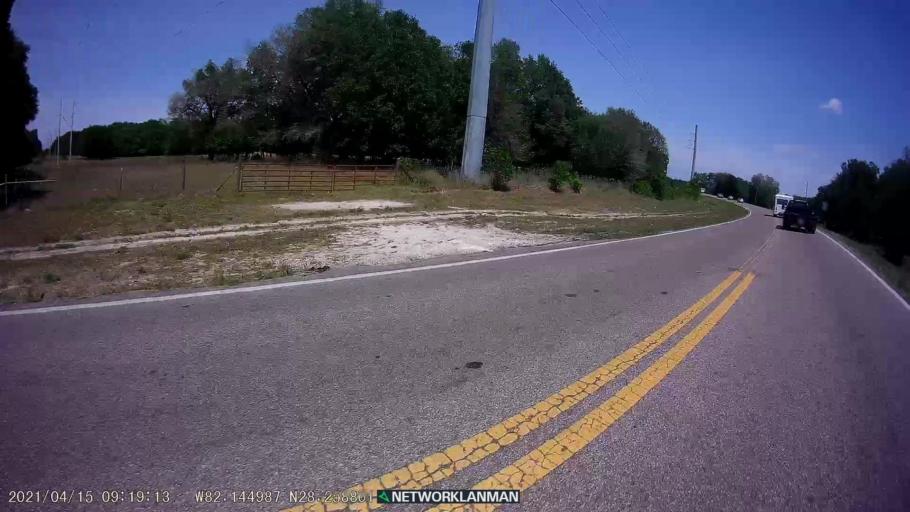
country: US
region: Florida
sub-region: Pasco County
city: Zephyrhills North
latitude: 28.2592
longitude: -82.1448
